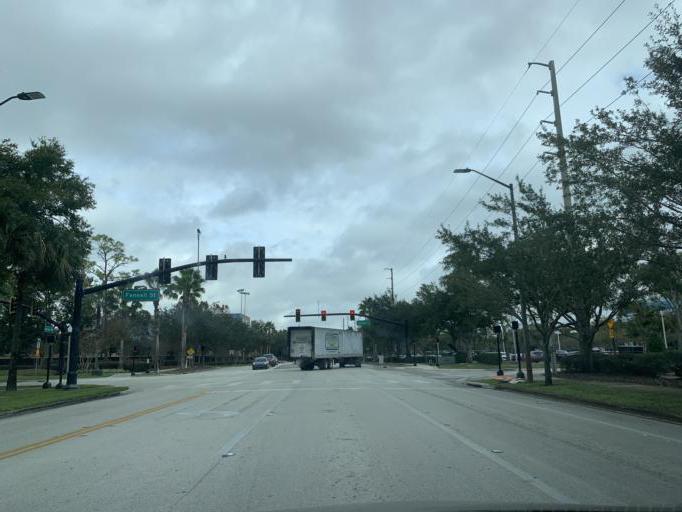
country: US
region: Florida
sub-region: Orange County
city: Eatonville
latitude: 28.6271
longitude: -81.3984
